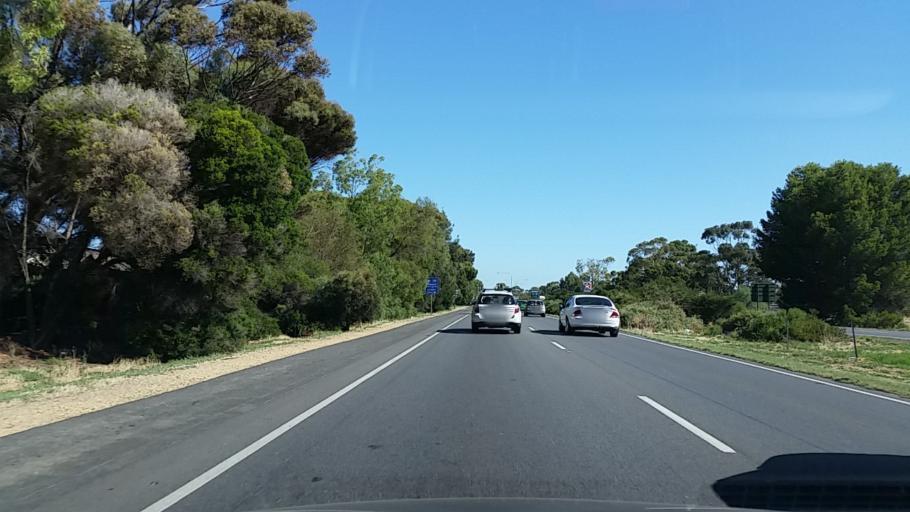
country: AU
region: South Australia
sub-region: Salisbury
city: Salisbury
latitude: -34.7561
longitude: 138.5906
